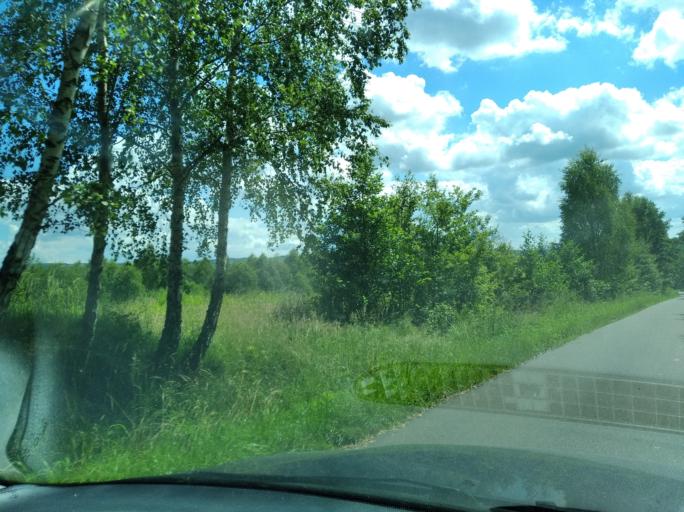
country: PL
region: Subcarpathian Voivodeship
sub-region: Powiat strzyzowski
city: Jawornik
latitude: 49.8572
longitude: 21.8893
